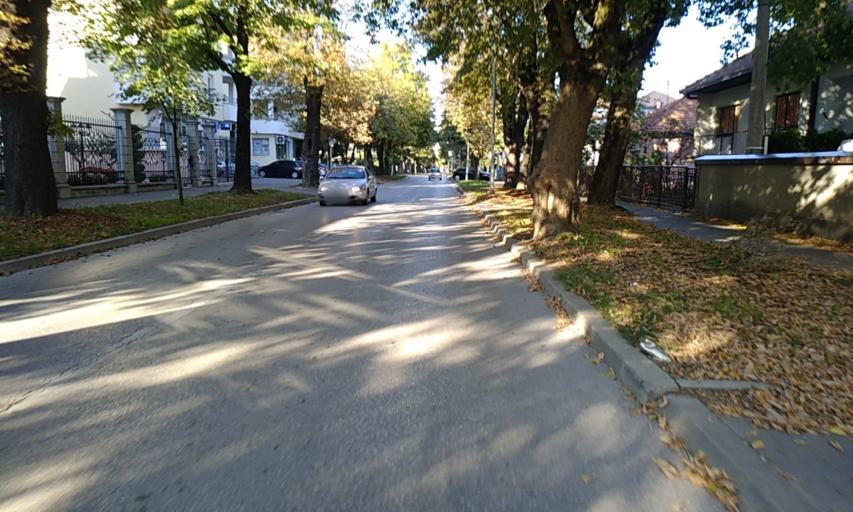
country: BA
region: Republika Srpska
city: Banja Luka
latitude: 44.7769
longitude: 17.1890
